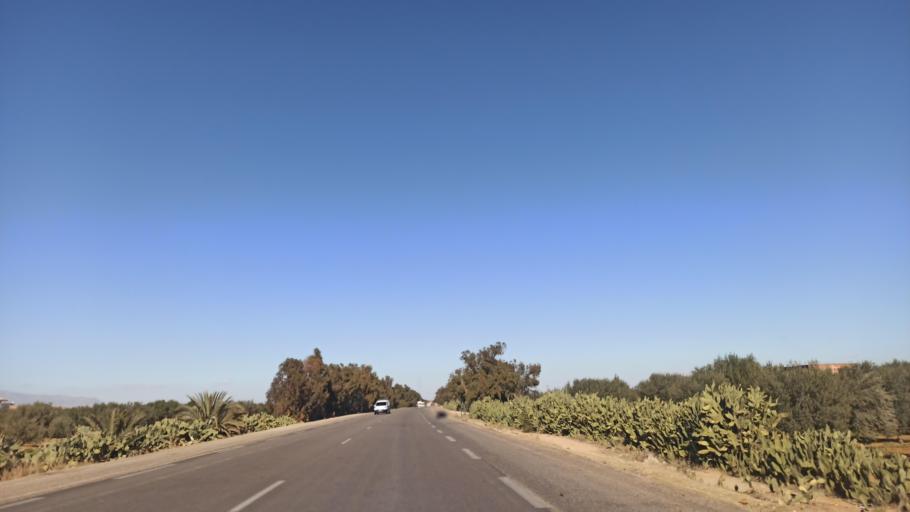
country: TN
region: Sidi Bu Zayd
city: Jilma
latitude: 35.1530
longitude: 9.3647
